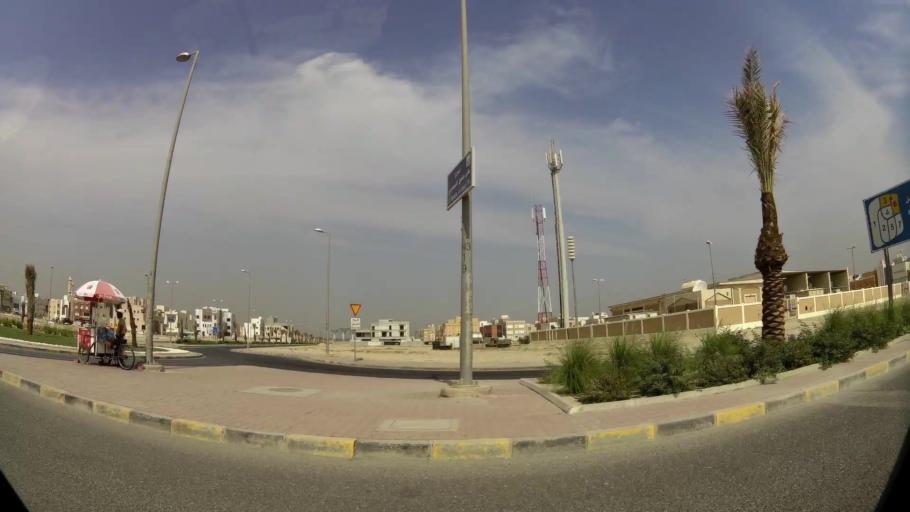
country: KW
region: Al Farwaniyah
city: Janub as Surrah
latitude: 29.2905
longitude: 47.9985
